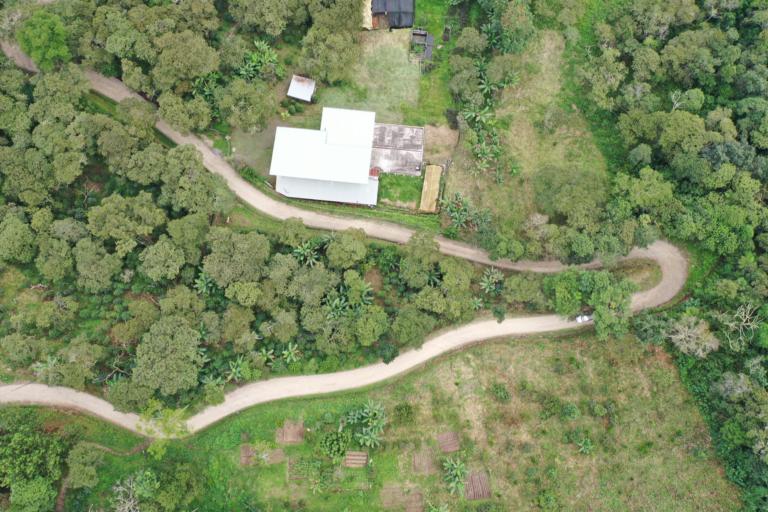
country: BO
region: La Paz
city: Coroico
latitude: -16.2597
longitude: -67.6932
